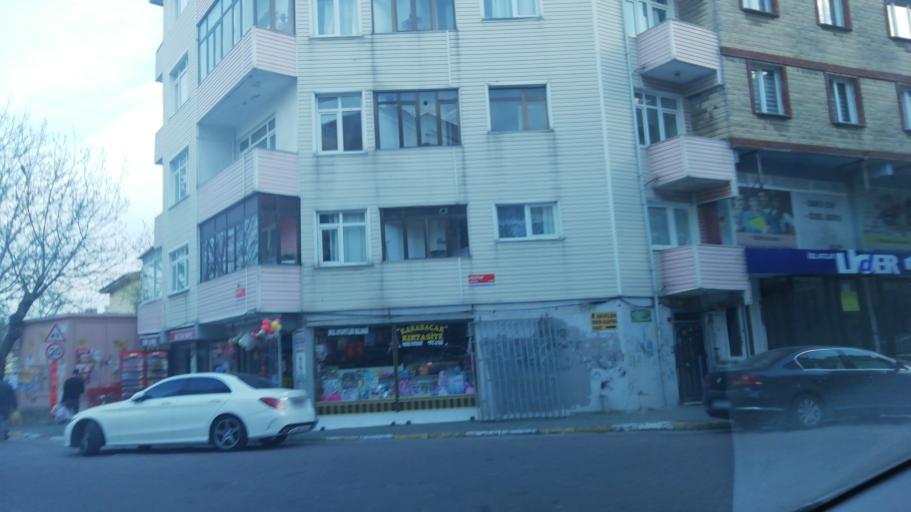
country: TR
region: Istanbul
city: Yakuplu
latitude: 40.9759
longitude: 28.7341
